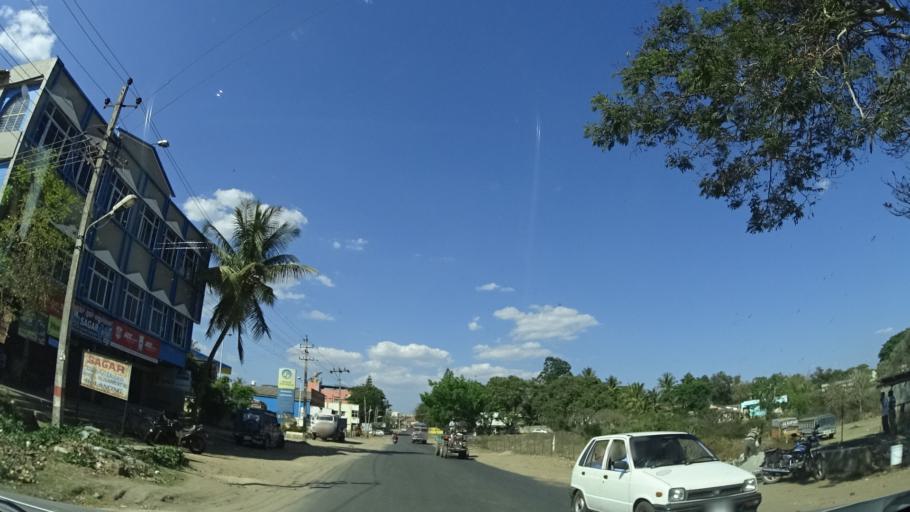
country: IN
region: Karnataka
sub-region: Chikmagalur
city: Chikmagalur
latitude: 13.3103
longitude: 75.7696
